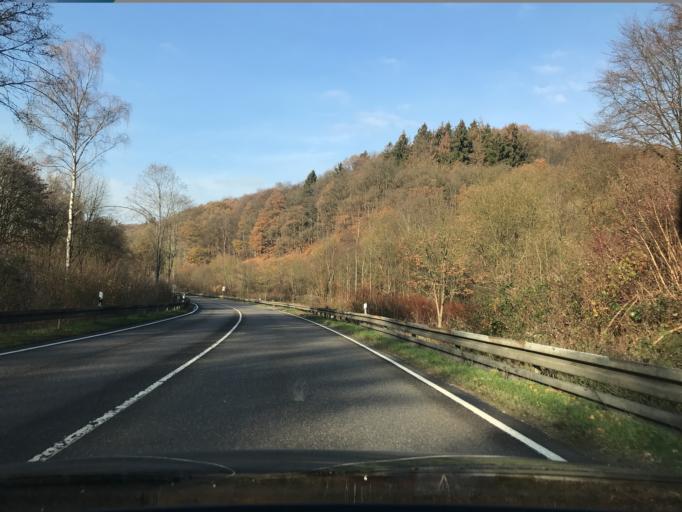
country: DE
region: North Rhine-Westphalia
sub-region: Regierungsbezirk Dusseldorf
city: Solingen
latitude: 51.1828
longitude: 7.1265
